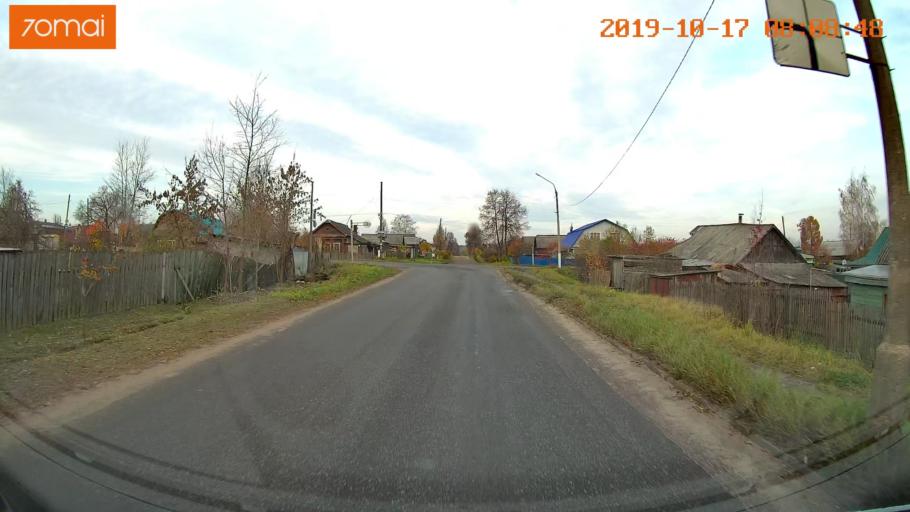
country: RU
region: Vladimir
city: Kol'chugino
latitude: 56.3153
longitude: 39.3834
